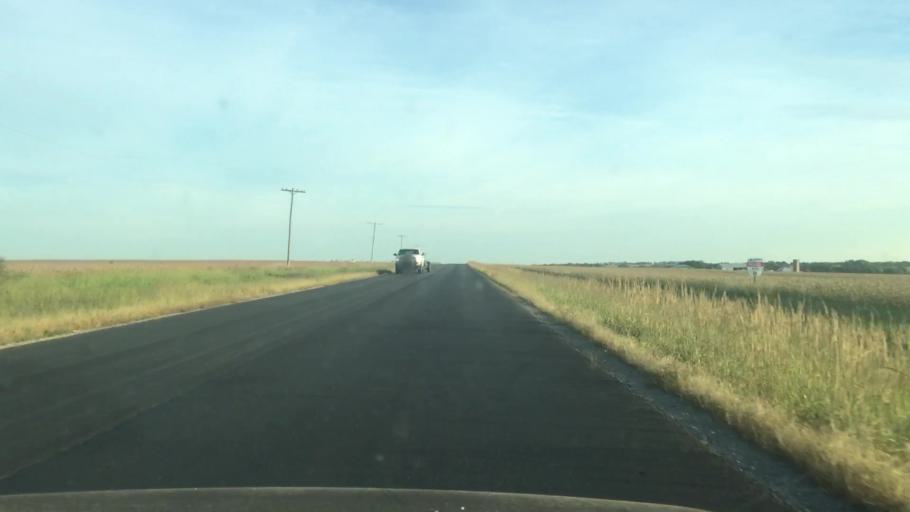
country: US
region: Kansas
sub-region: Marshall County
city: Marysville
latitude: 39.8646
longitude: -96.6009
